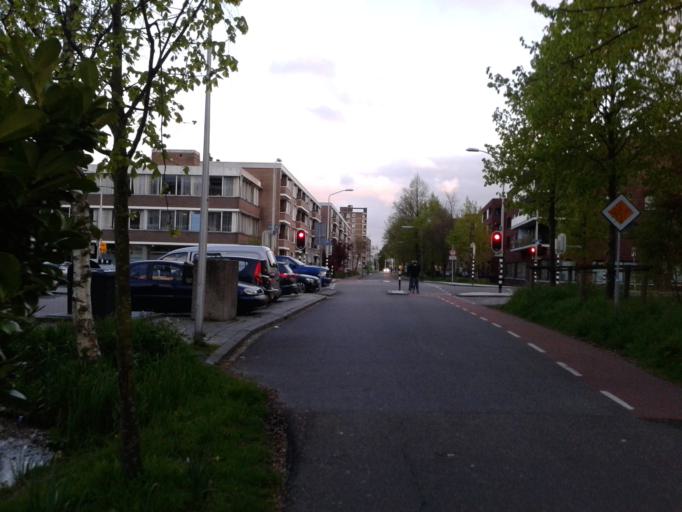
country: NL
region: South Holland
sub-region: Gemeente Gouda
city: Gouda
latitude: 52.0210
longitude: 4.7086
